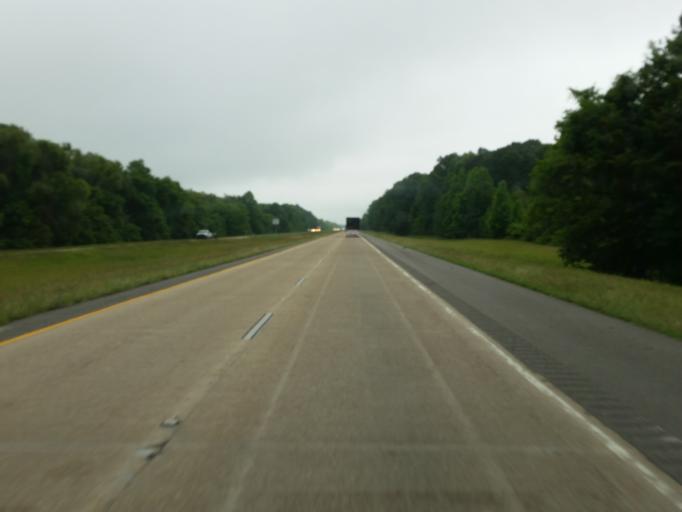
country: US
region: Louisiana
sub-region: Madison Parish
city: Tallulah
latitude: 32.3508
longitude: -91.0915
